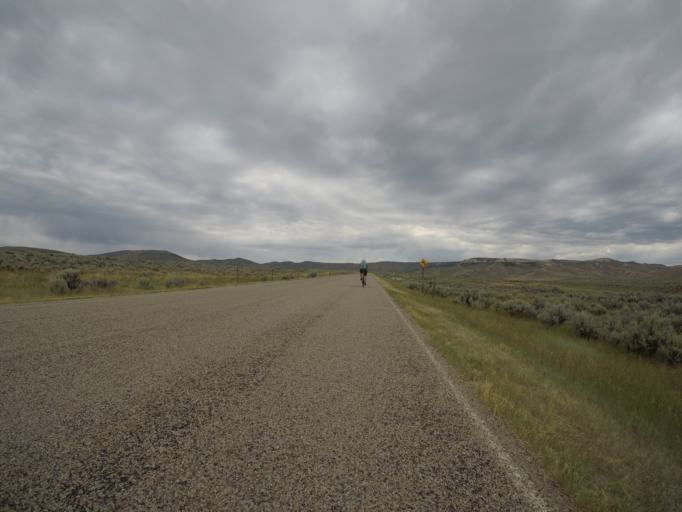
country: US
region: Wyoming
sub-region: Lincoln County
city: Kemmerer
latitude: 41.8316
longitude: -110.7703
